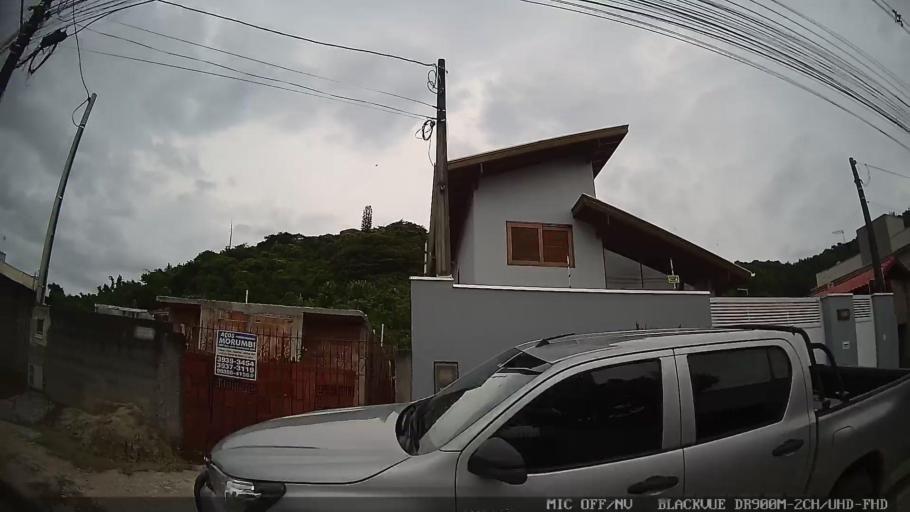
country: BR
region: Sao Paulo
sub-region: Caraguatatuba
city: Caraguatatuba
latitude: -23.6228
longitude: -45.3904
